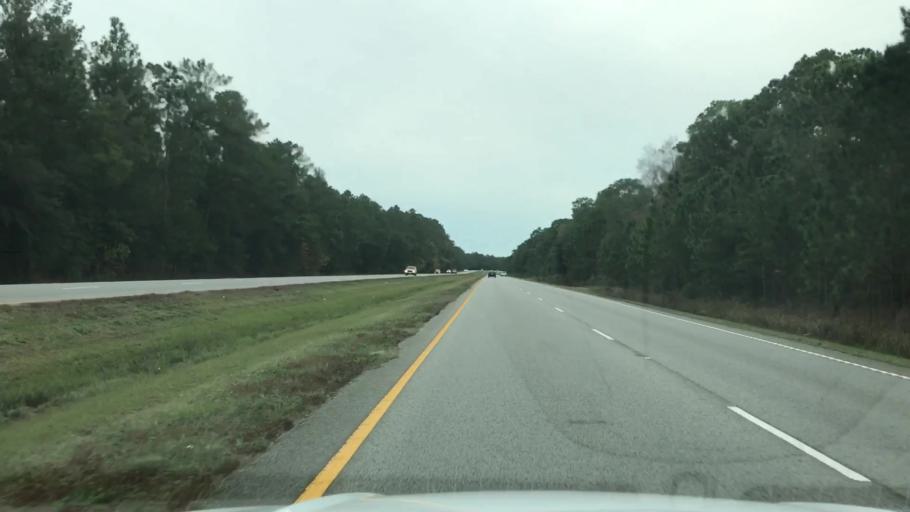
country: US
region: South Carolina
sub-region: Georgetown County
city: Georgetown
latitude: 33.3936
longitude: -79.2029
